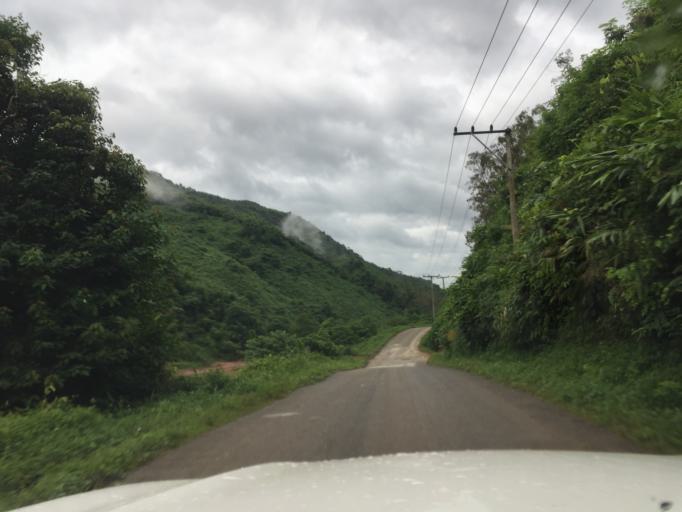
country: LA
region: Oudomxai
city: Muang La
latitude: 20.9959
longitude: 102.2309
